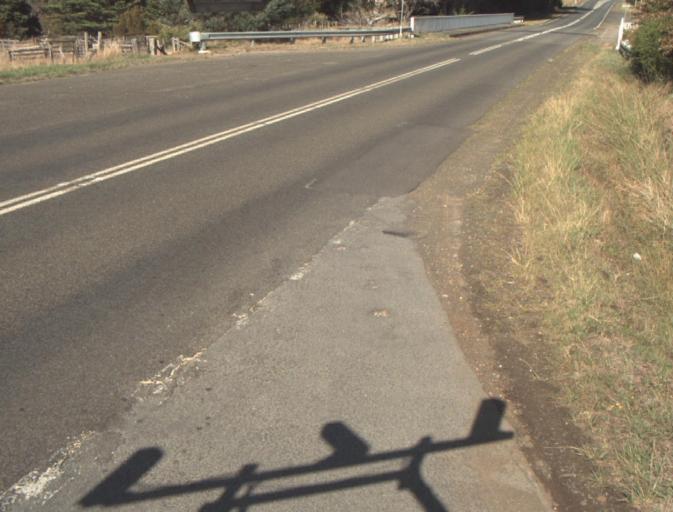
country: AU
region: Tasmania
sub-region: Launceston
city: Mayfield
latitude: -41.3301
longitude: 147.0718
